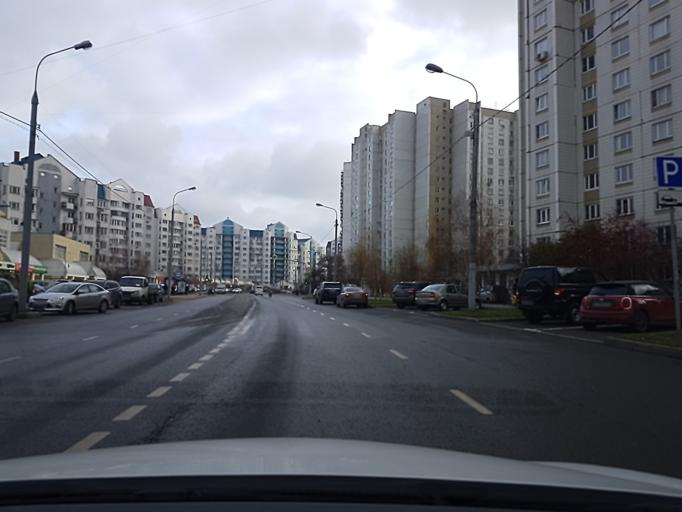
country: RU
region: Moskovskaya
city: Pavshino
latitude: 55.8364
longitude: 37.3542
